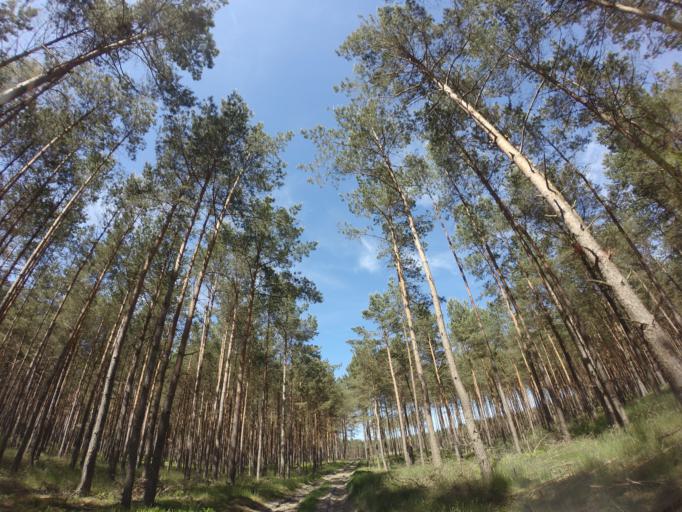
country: PL
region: West Pomeranian Voivodeship
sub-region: Powiat choszczenski
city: Drawno
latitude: 53.1334
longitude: 15.7894
